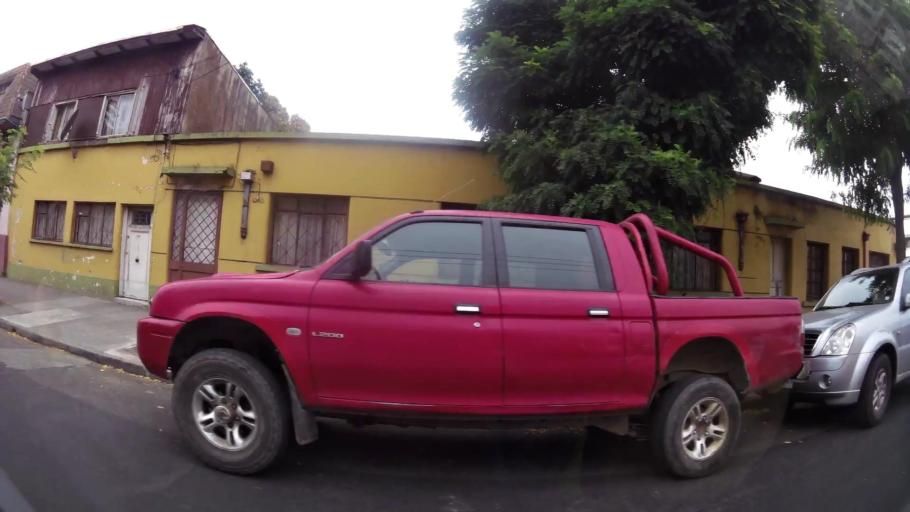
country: CL
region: Biobio
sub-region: Provincia de Concepcion
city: Concepcion
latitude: -36.8227
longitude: -73.0597
